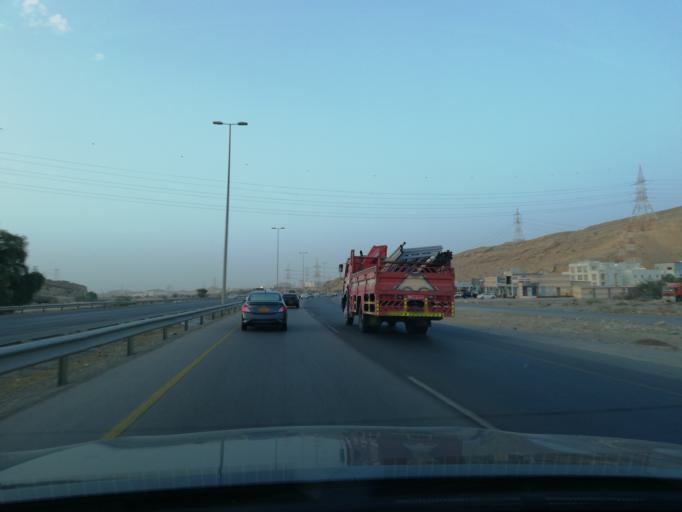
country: OM
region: Muhafazat Masqat
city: As Sib al Jadidah
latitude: 23.5441
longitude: 58.1893
